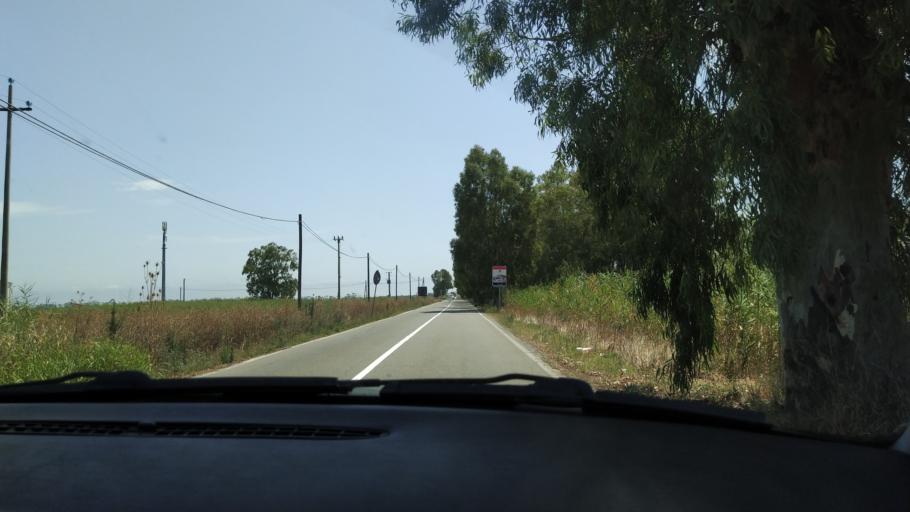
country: IT
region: Basilicate
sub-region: Provincia di Matera
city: Marconia
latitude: 40.3393
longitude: 16.7652
